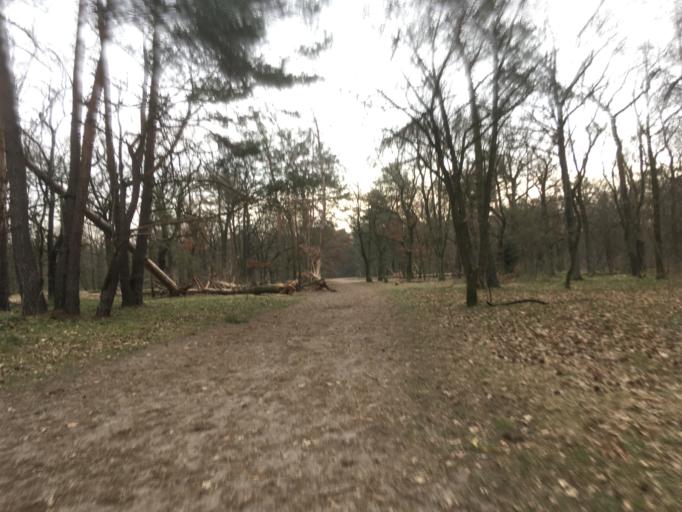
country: DE
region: Berlin
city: Baumschulenweg
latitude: 52.4549
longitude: 13.4904
